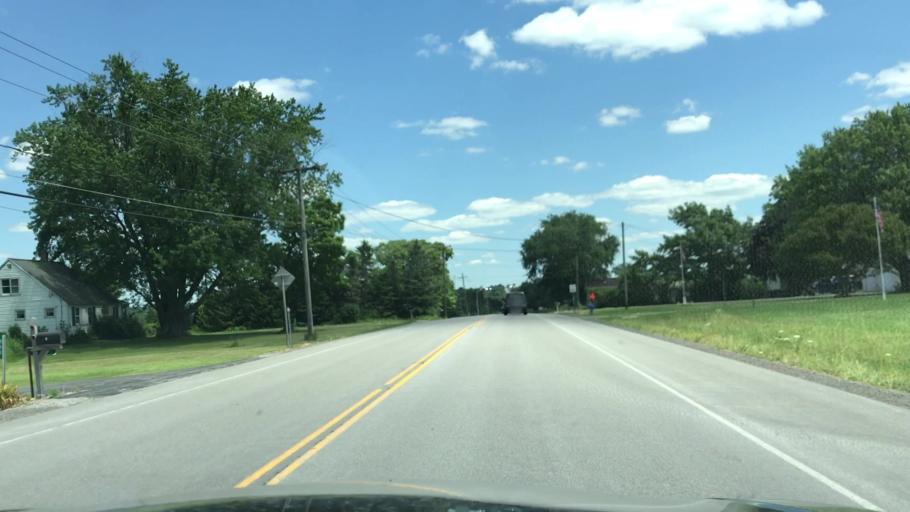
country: US
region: New York
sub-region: Erie County
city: Alden
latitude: 42.7695
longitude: -78.4604
